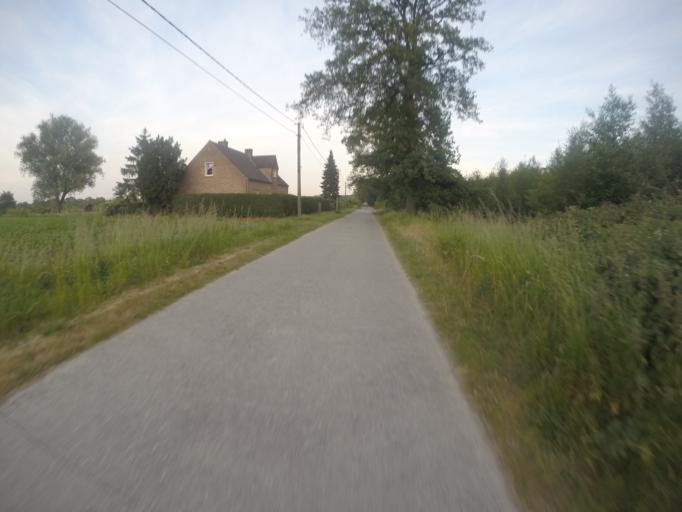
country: BE
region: Flanders
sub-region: Provincie Oost-Vlaanderen
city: Zomergem
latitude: 51.1317
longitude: 3.5150
